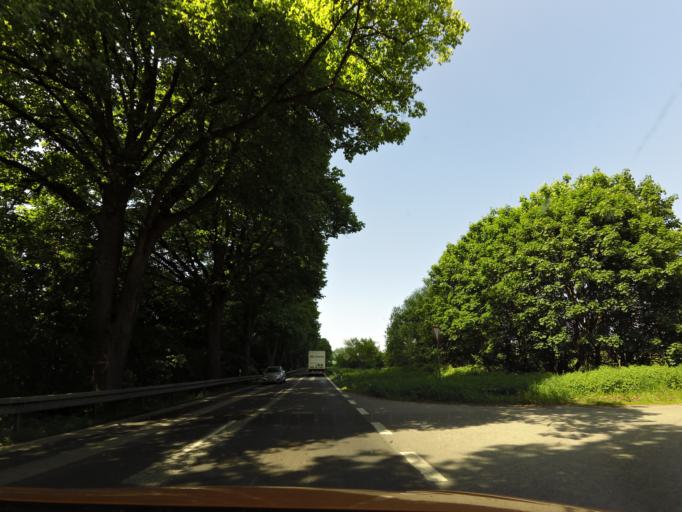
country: DE
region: Mecklenburg-Vorpommern
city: Selmsdorf
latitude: 53.8691
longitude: 10.8957
